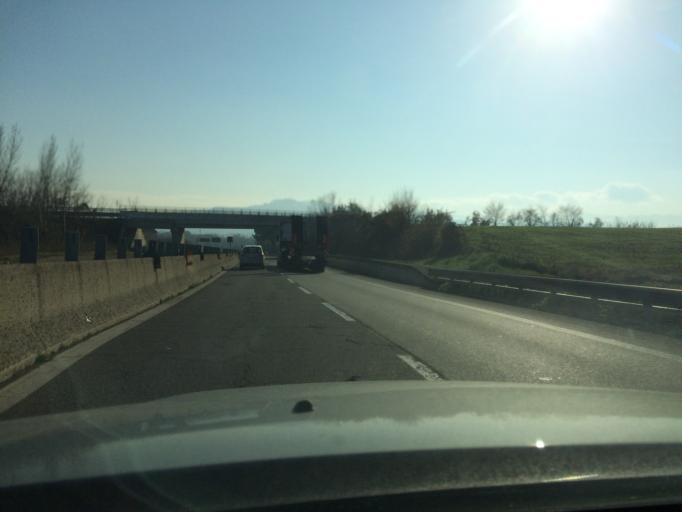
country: IT
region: Umbria
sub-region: Provincia di Perugia
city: Ponterio-Pian di Porto
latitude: 42.8218
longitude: 12.3995
